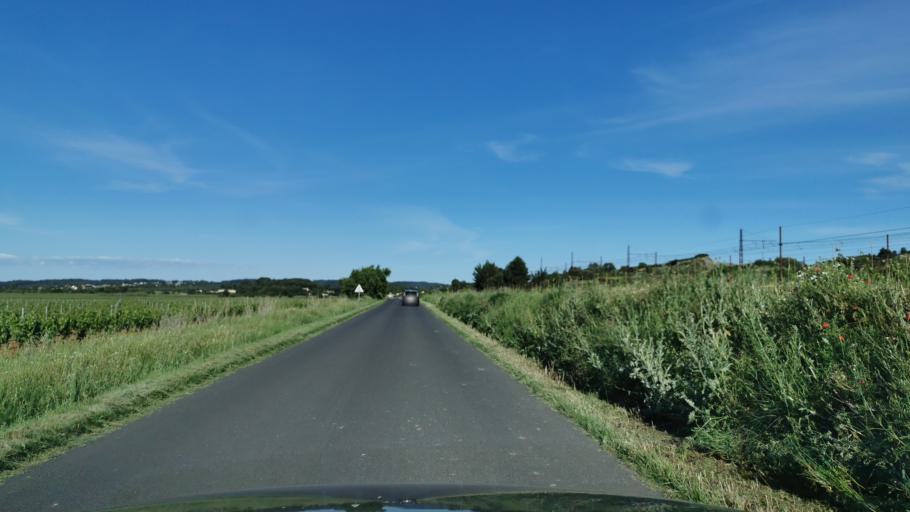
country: FR
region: Languedoc-Roussillon
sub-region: Departement de l'Aude
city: Nevian
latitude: 43.2138
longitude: 2.8833
